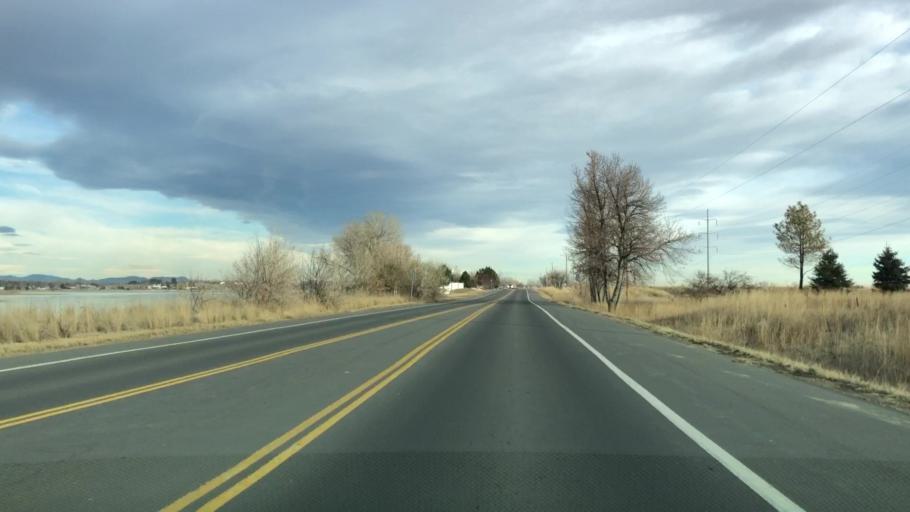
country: US
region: Colorado
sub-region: Larimer County
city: Loveland
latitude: 40.4327
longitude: -105.0454
